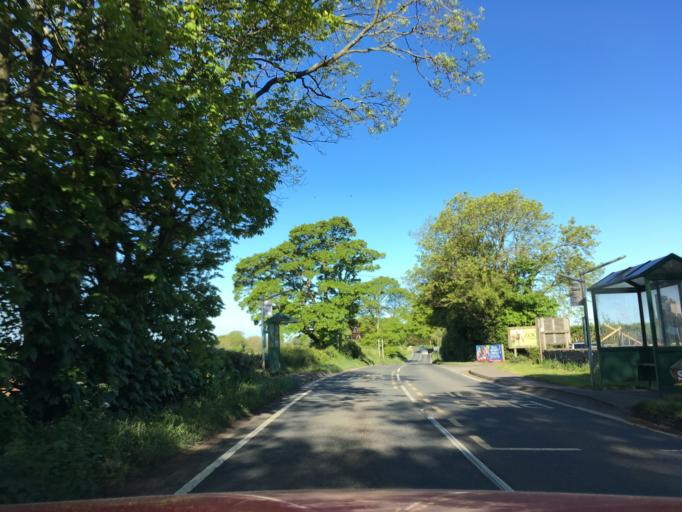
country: GB
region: England
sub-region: North Somerset
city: Nailsea
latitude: 51.4508
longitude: -2.7379
